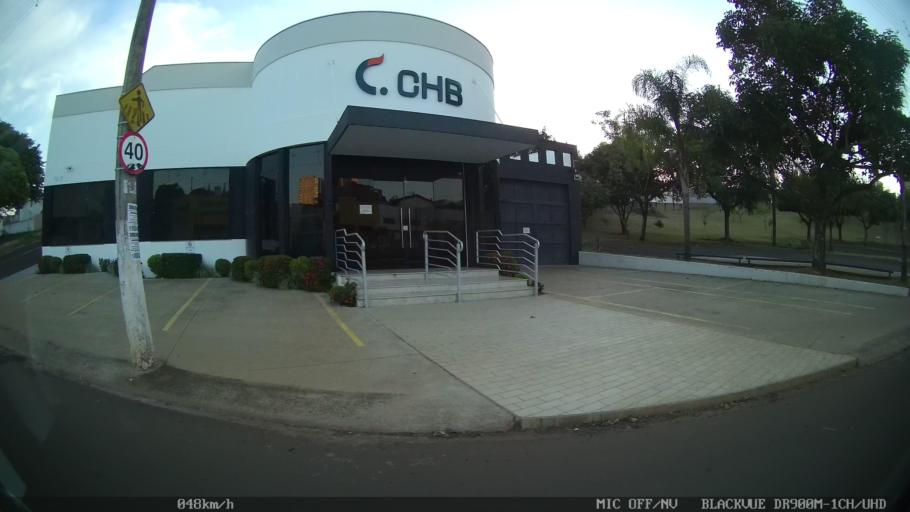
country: BR
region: Sao Paulo
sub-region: Franca
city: Franca
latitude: -20.5428
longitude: -47.4084
